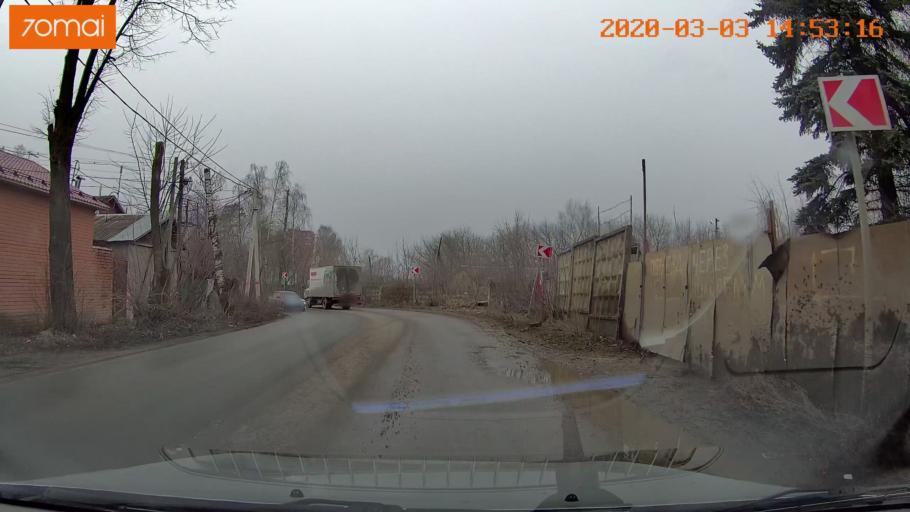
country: RU
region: Moskovskaya
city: Korenevo
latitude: 55.6741
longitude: 38.0106
